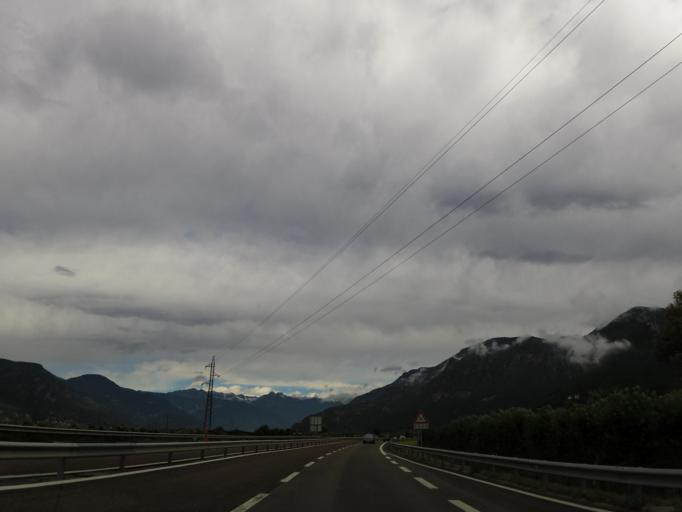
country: IT
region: Trentino-Alto Adige
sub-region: Bolzano
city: Cornaiano
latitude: 46.4884
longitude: 11.2872
